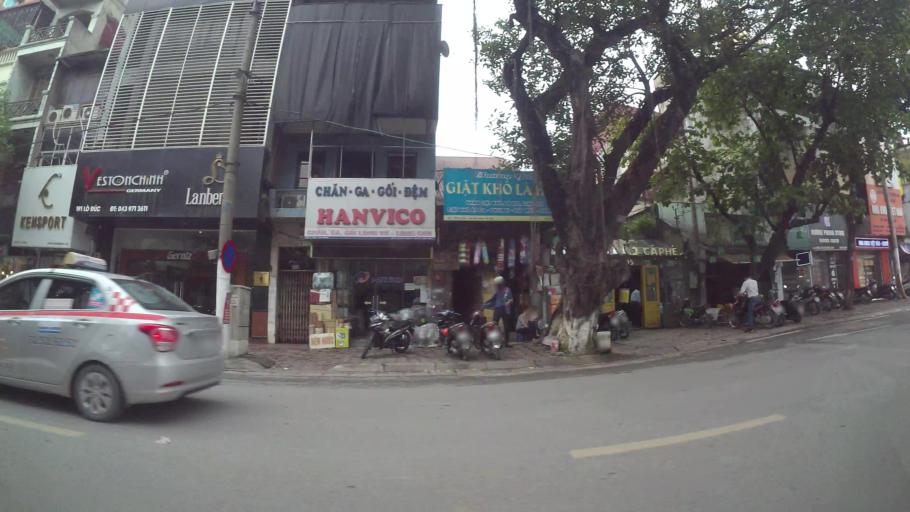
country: VN
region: Ha Noi
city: Hai BaTrung
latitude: 21.0096
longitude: 105.8608
